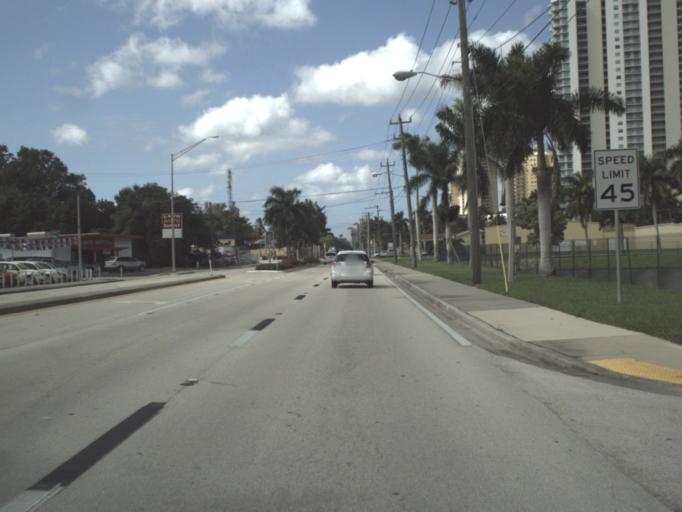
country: US
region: Florida
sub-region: Lee County
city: North Fort Myers
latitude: 26.6553
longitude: -81.8503
